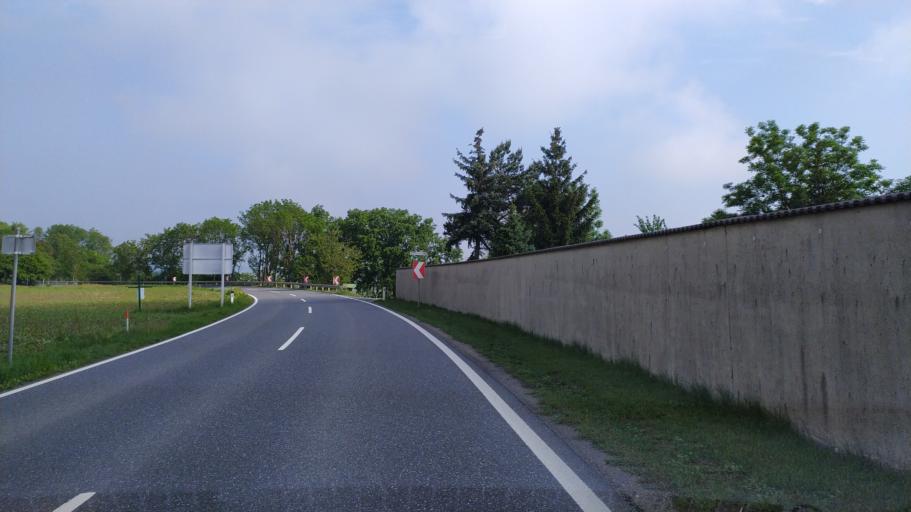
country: AT
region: Lower Austria
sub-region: Politischer Bezirk Amstetten
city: Ennsdorf
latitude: 48.2048
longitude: 14.5517
